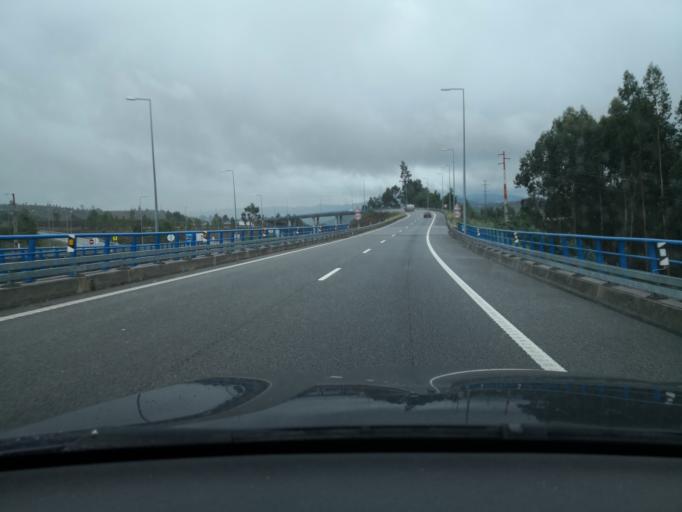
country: PT
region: Porto
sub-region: Valongo
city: Sobrado
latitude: 41.2308
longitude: -8.4595
